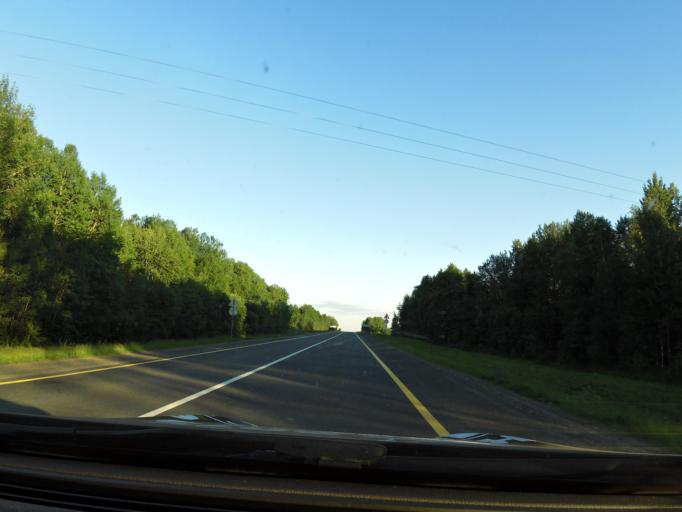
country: RU
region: Vologda
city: Gryazovets
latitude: 58.7800
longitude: 40.2726
